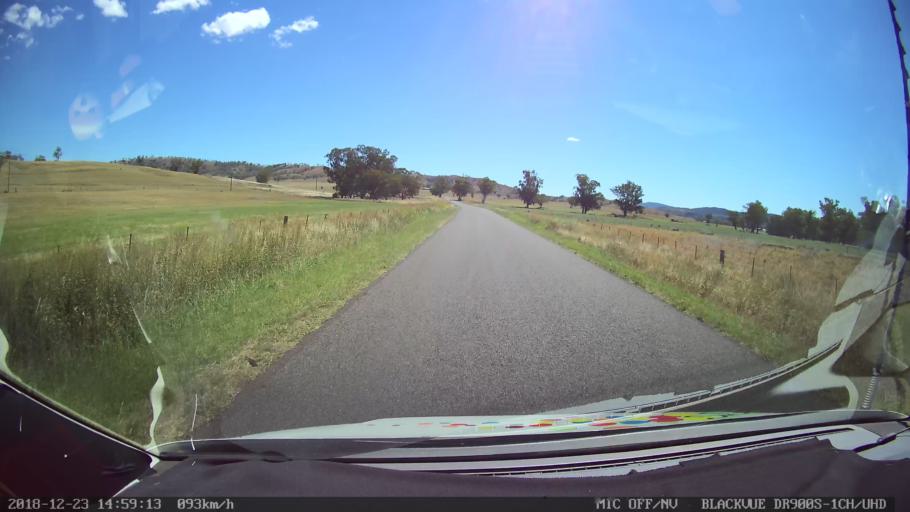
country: AU
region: New South Wales
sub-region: Tamworth Municipality
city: Manilla
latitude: -30.7223
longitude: 150.8036
